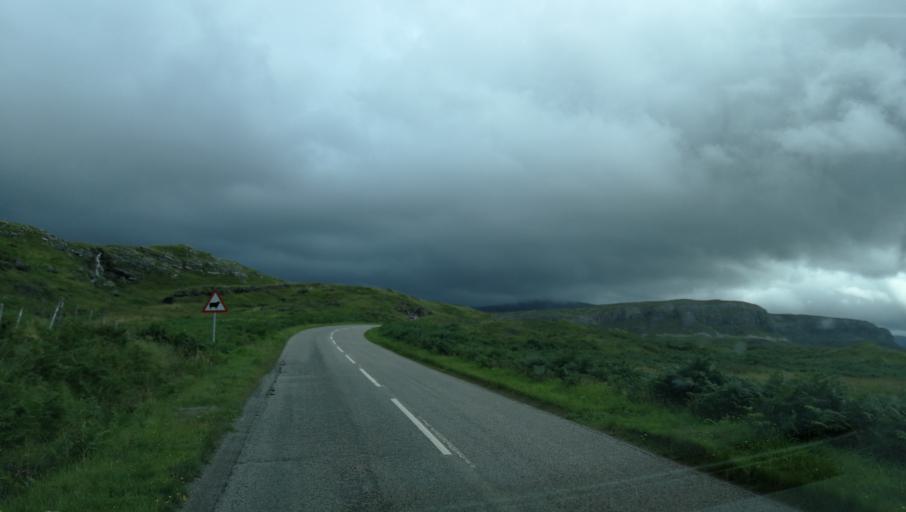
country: GB
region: Scotland
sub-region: Highland
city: Ullapool
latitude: 58.1586
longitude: -4.9796
